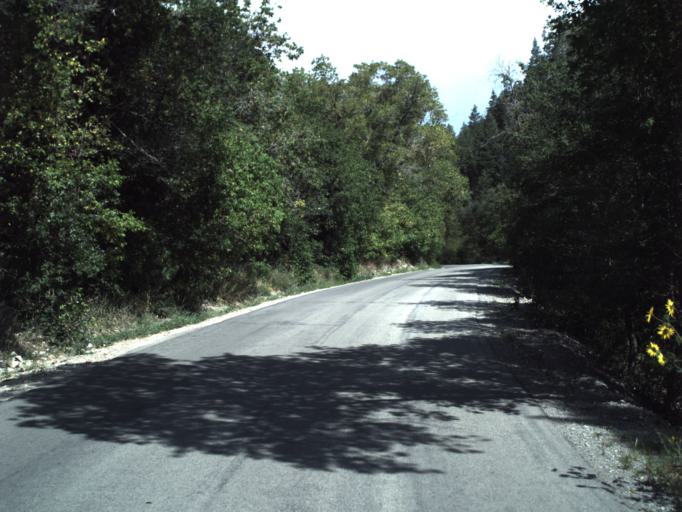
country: US
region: Utah
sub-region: Utah County
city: Cedar Hills
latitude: 40.4674
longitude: -111.6553
